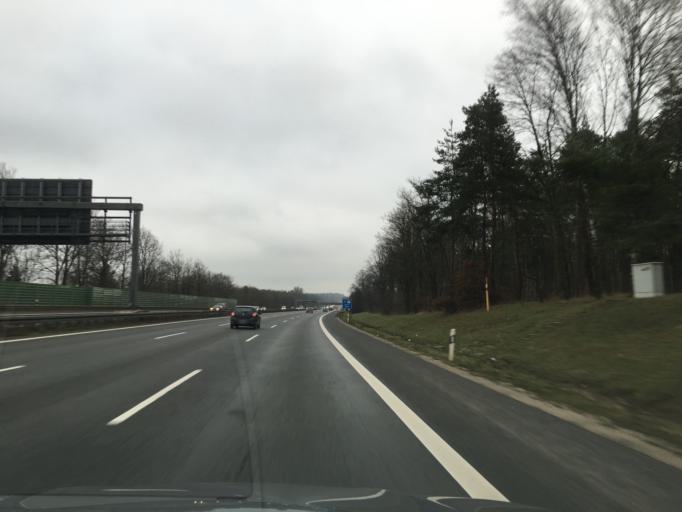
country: DE
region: Bavaria
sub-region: Regierungsbezirk Mittelfranken
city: Feucht
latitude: 49.4145
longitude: 11.1986
